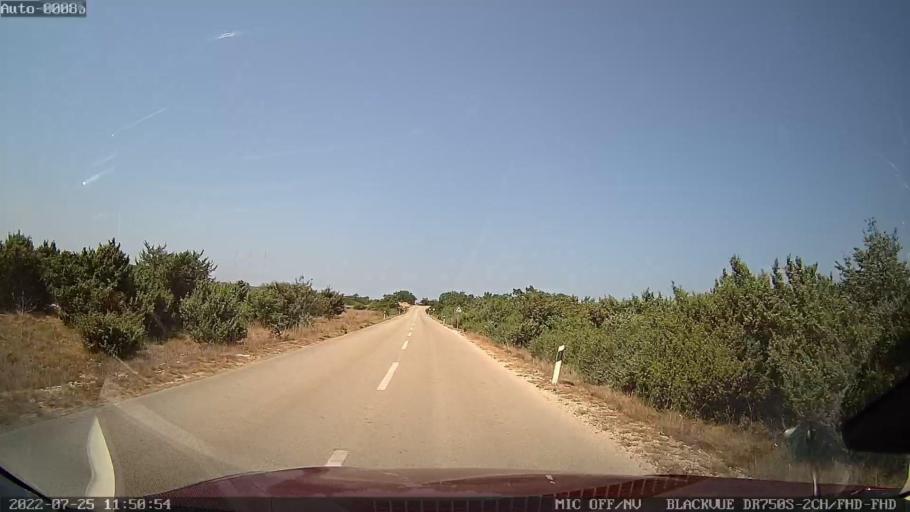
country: HR
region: Zadarska
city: Vrsi
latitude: 44.2376
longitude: 15.2585
